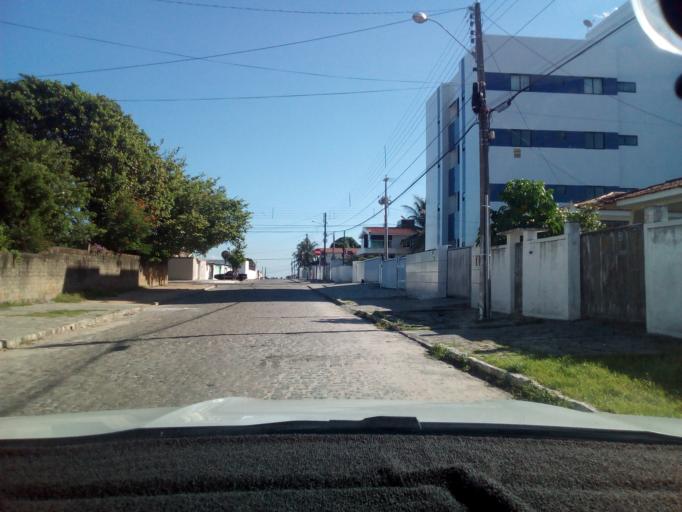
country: BR
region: Paraiba
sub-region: Joao Pessoa
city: Joao Pessoa
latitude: -7.1529
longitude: -34.8800
